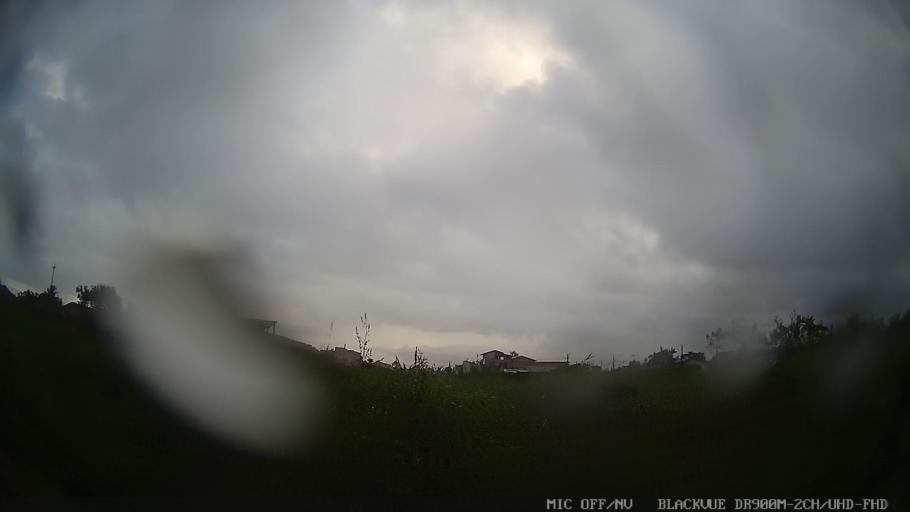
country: BR
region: Sao Paulo
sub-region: Itanhaem
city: Itanhaem
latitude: -24.1999
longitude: -46.8307
